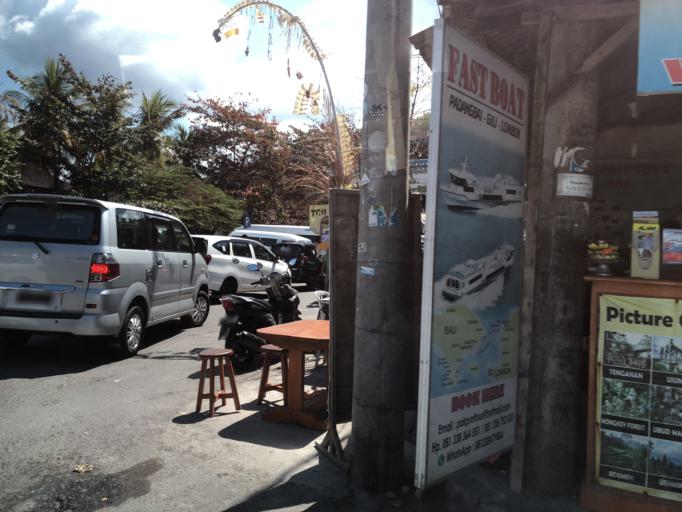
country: ID
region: Bali
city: Padangbai
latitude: -8.5308
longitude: 115.5093
